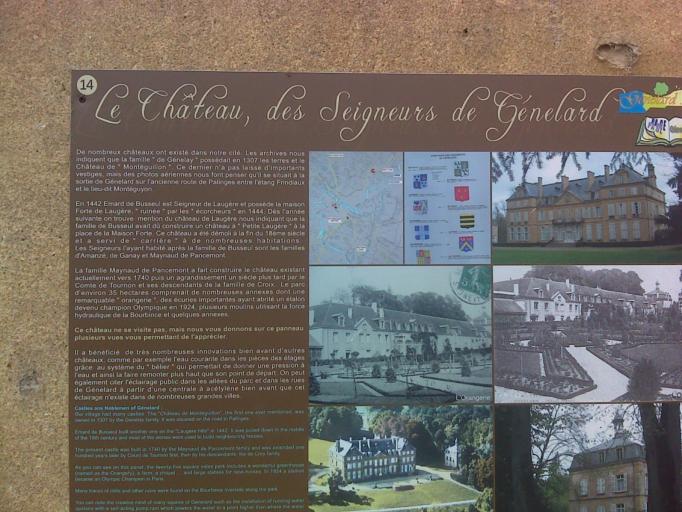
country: FR
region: Bourgogne
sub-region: Departement de Saone-et-Loire
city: Genelard
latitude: 46.5830
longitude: 4.2343
